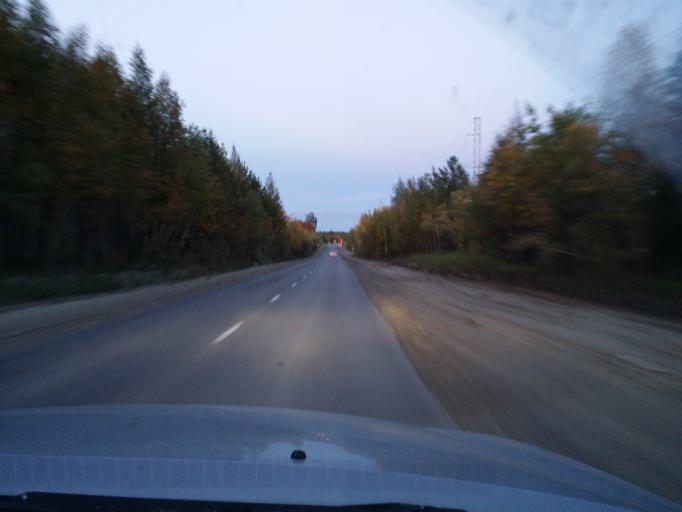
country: RU
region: Khanty-Mansiyskiy Avtonomnyy Okrug
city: Nizhnevartovsk
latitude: 60.9923
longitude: 76.4224
